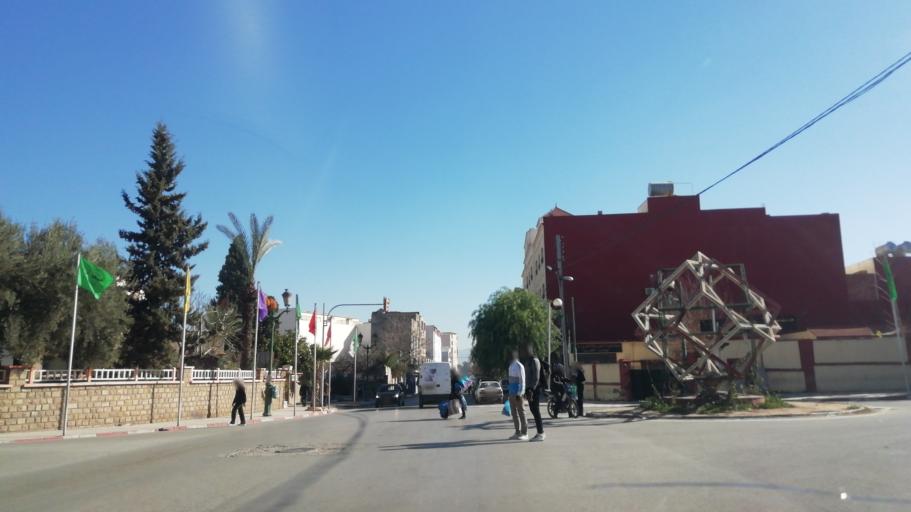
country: DZ
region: Tlemcen
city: Nedroma
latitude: 34.8462
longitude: -1.7272
